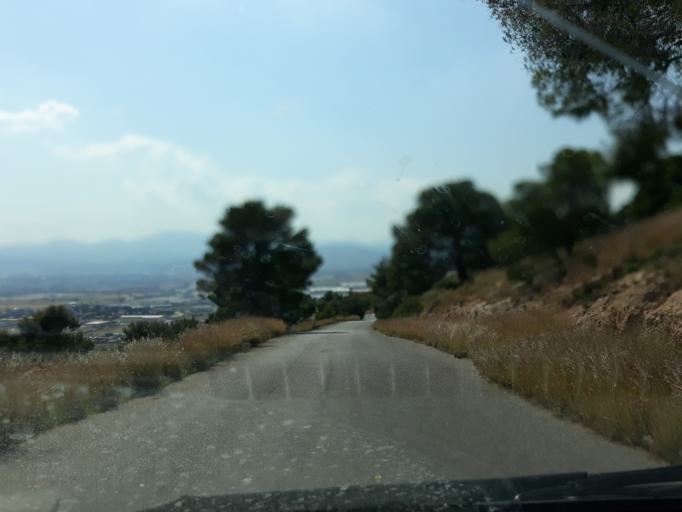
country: GR
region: Attica
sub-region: Nomarchia Dytikis Attikis
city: Fyli
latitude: 38.0941
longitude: 23.6376
